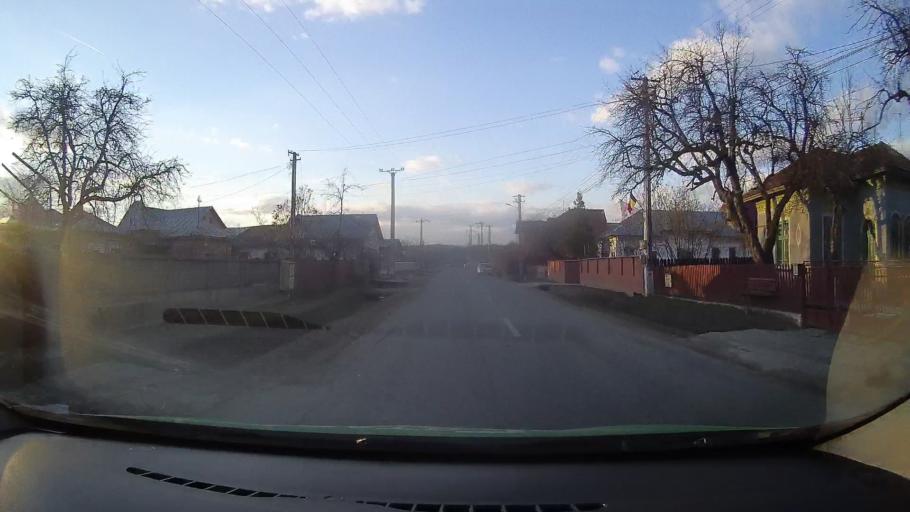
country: RO
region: Dambovita
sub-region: Comuna Gura Ocnitei
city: Adanca
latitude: 44.9289
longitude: 25.6029
